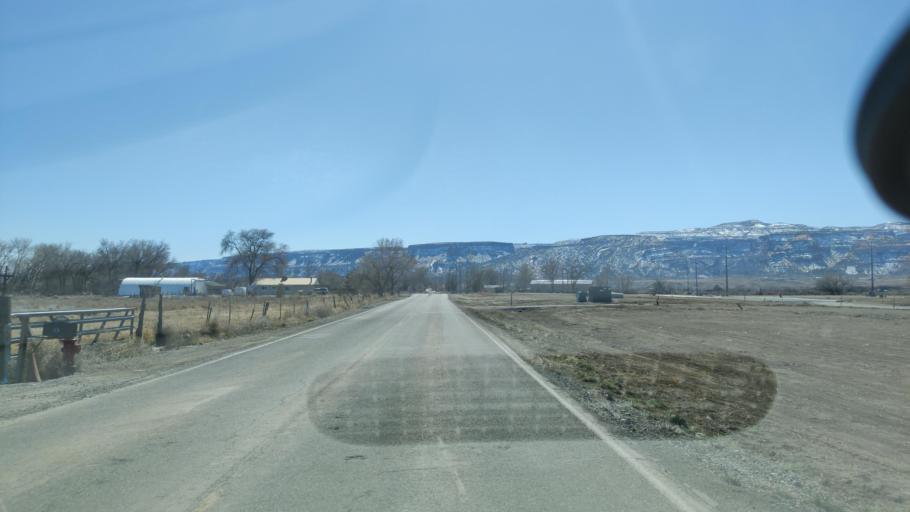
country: US
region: Colorado
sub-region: Mesa County
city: Fruita
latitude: 39.1445
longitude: -108.7012
